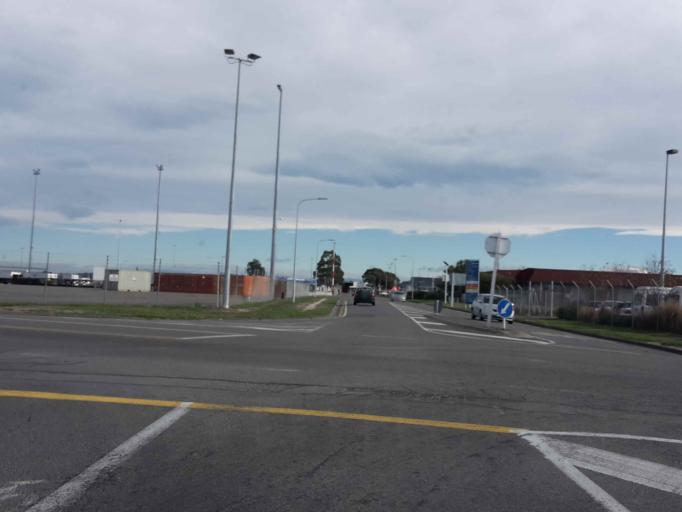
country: NZ
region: Canterbury
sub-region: Christchurch City
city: Christchurch
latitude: -43.4856
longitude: 172.5497
